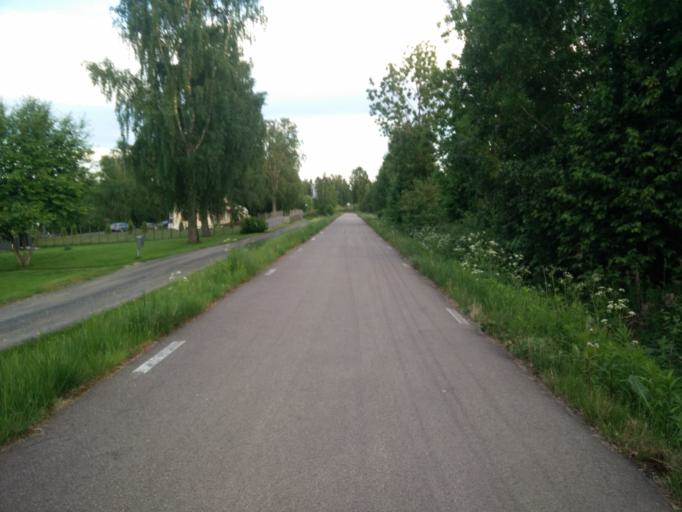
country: SE
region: Vaermland
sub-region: Hagfors Kommun
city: Hagfors
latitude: 60.0085
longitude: 13.6021
